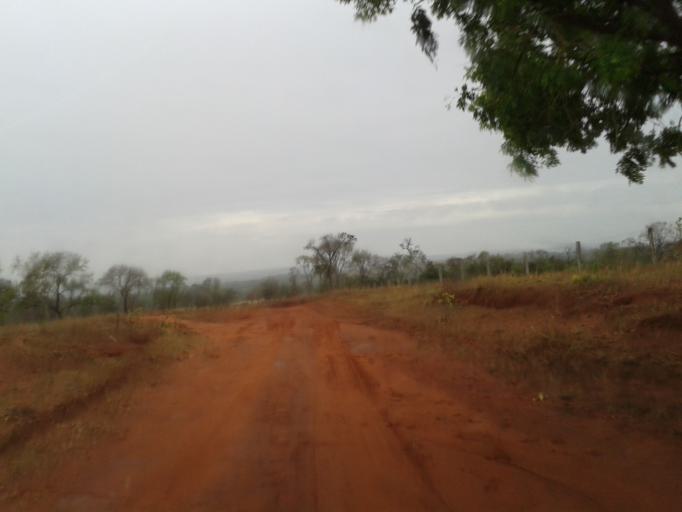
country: BR
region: Minas Gerais
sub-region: Campina Verde
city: Campina Verde
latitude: -19.3070
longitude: -49.5052
